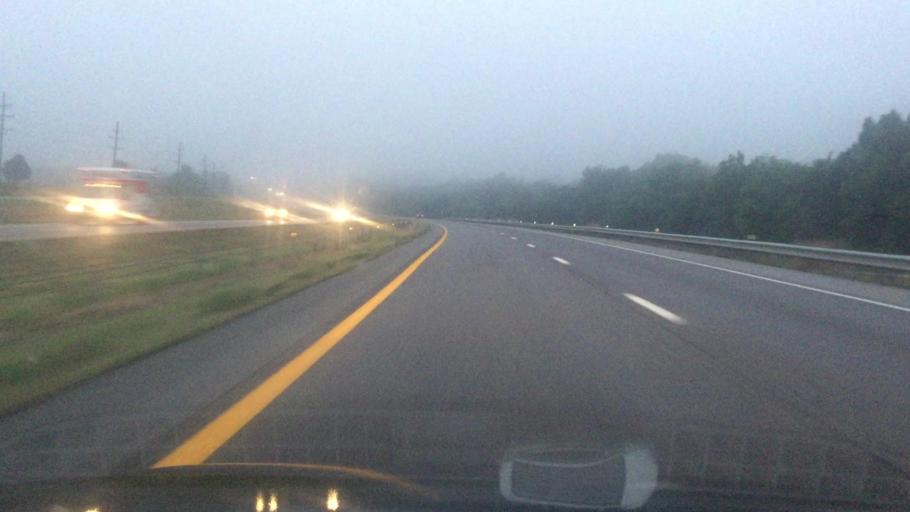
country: US
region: Missouri
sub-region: Warren County
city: Warrenton
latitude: 38.8458
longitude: -91.2367
